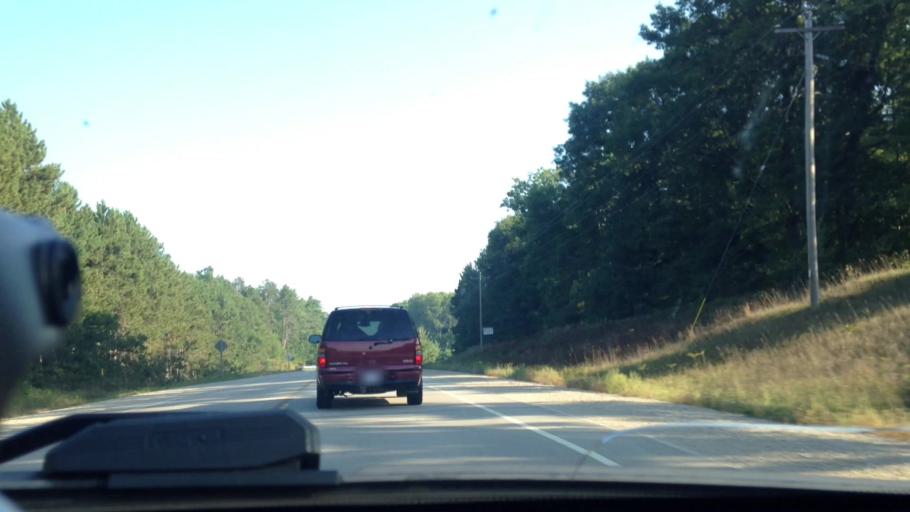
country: US
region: Wisconsin
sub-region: Marinette County
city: Peshtigo
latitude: 45.1669
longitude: -87.9963
